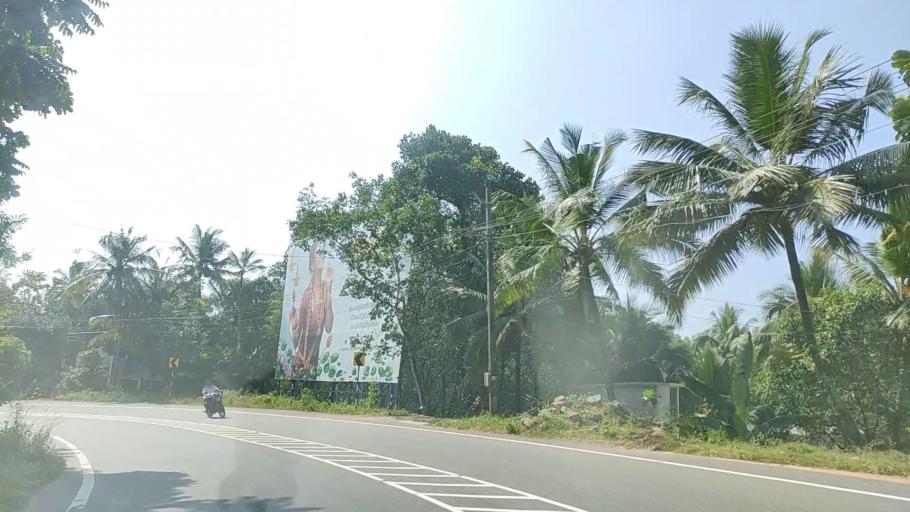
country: IN
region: Kerala
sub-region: Kollam
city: Punalur
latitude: 8.9310
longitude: 76.9993
